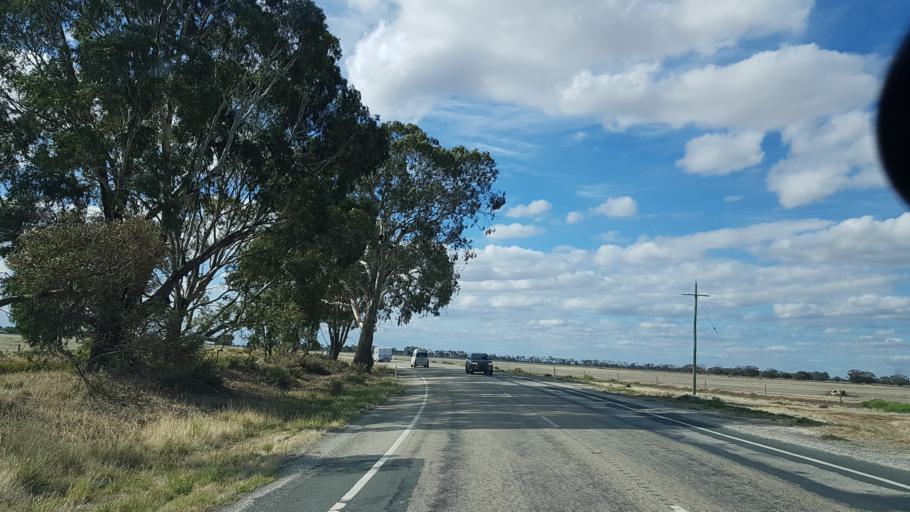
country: AU
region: Victoria
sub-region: Swan Hill
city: Swan Hill
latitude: -35.8125
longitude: 143.9558
